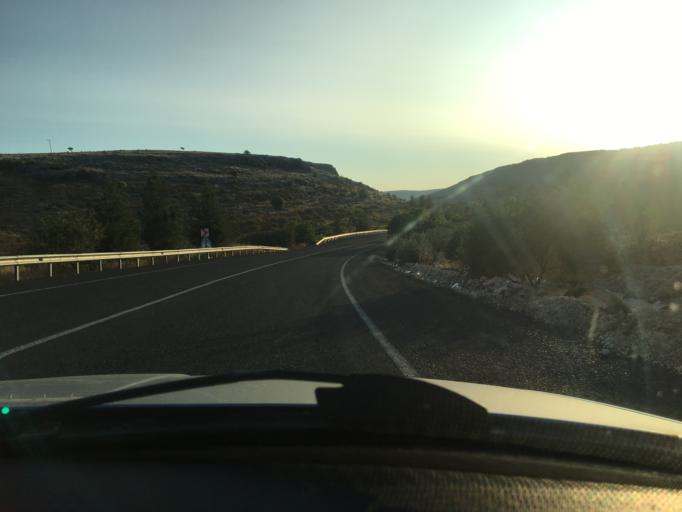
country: TR
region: Sanliurfa
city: Halfeti
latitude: 37.2235
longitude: 37.9593
